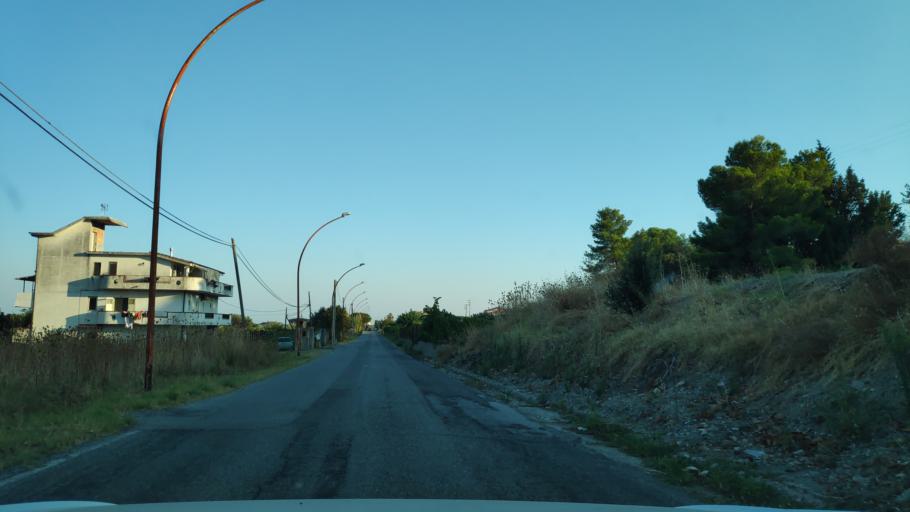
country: IT
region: Calabria
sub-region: Provincia di Reggio Calabria
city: Caulonia Marina
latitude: 38.3677
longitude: 16.4838
